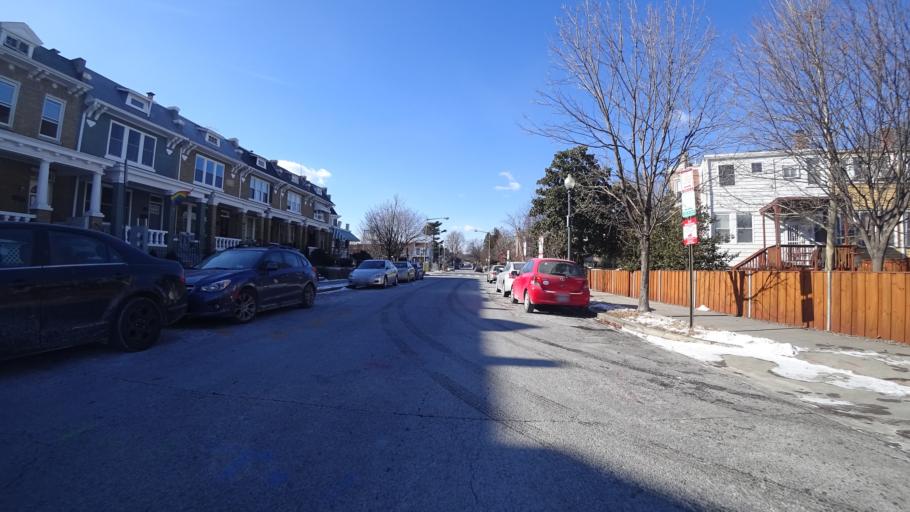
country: US
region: Washington, D.C.
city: Washington, D.C.
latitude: 38.9376
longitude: -77.0283
